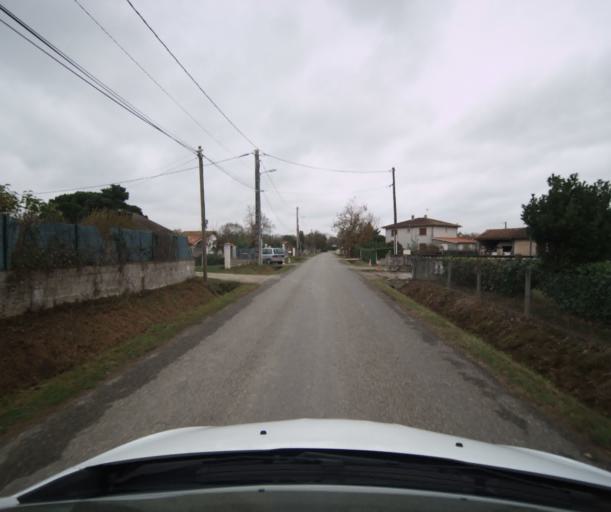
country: FR
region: Midi-Pyrenees
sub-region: Departement du Tarn-et-Garonne
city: Saint-Porquier
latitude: 44.0422
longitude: 1.1537
